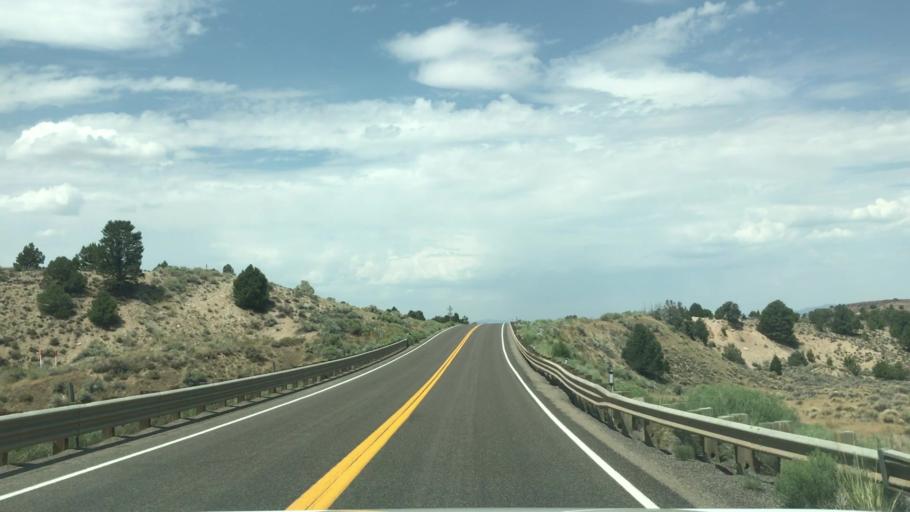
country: US
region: Nevada
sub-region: Eureka County
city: Eureka
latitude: 39.3911
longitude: -115.5028
